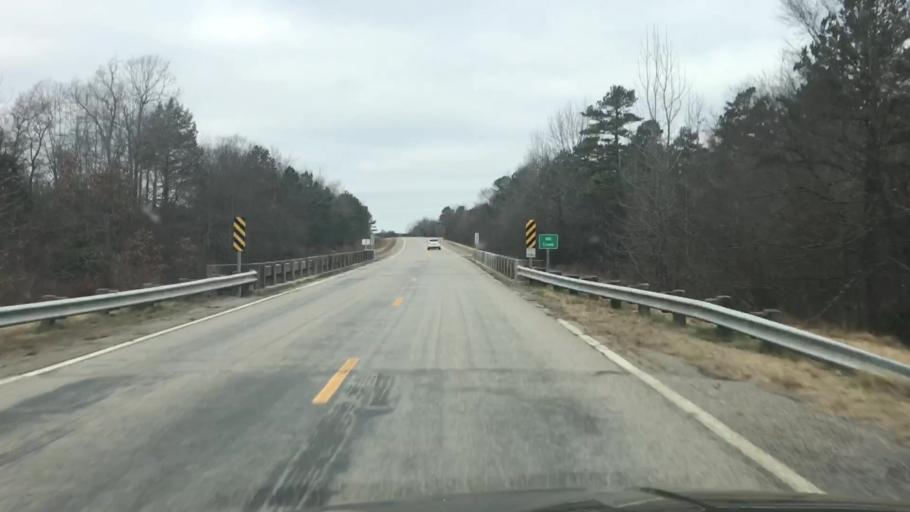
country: US
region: Arkansas
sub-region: Scott County
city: Waldron
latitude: 34.7013
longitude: -93.9167
